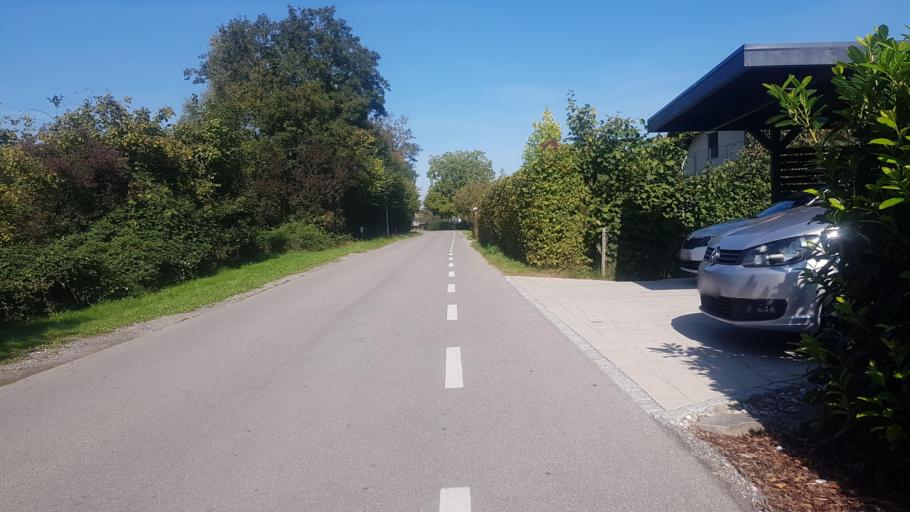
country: CH
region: Saint Gallen
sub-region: Wahlkreis Rheintal
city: Rheineck
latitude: 47.4750
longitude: 9.5888
